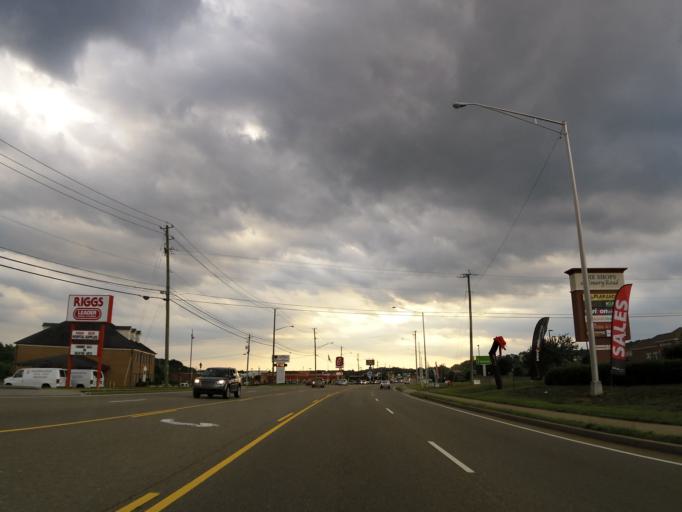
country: US
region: Tennessee
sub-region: Knox County
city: Knoxville
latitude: 36.0517
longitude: -83.9914
